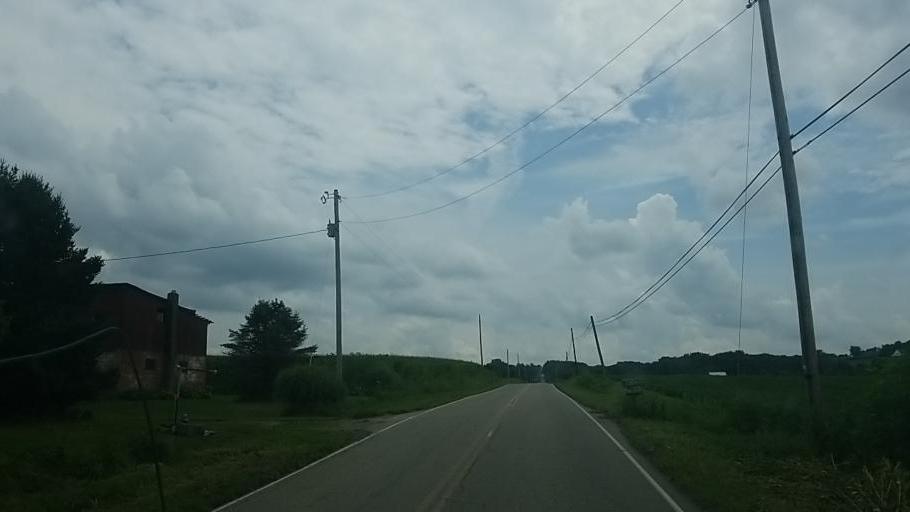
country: US
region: Ohio
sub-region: Licking County
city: Utica
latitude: 40.2312
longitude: -82.3653
